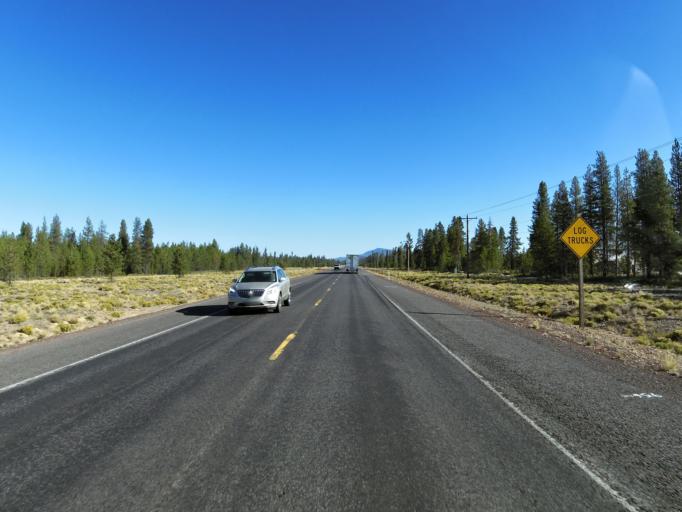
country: US
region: Oregon
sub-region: Deschutes County
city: La Pine
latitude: 43.1513
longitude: -121.7958
